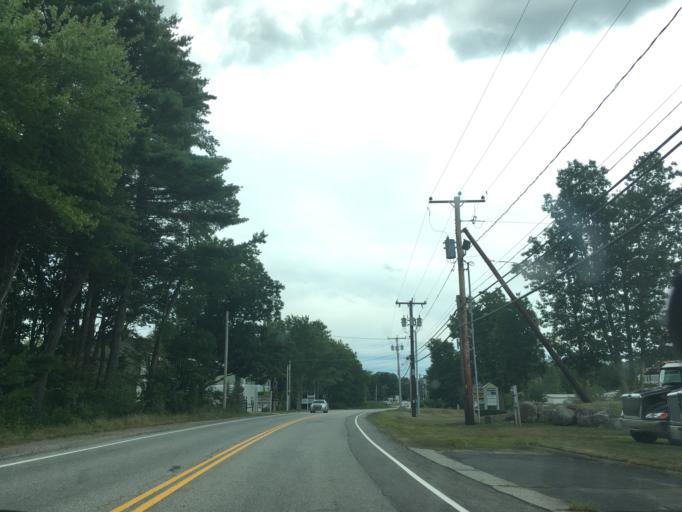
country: US
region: New Hampshire
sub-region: Rockingham County
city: Exeter
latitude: 42.9941
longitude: -70.9708
